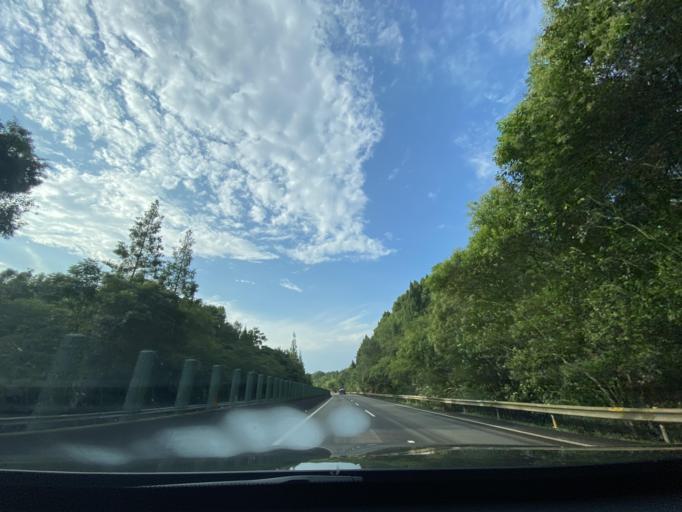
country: CN
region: Sichuan
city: Jiancheng
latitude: 30.3099
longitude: 104.5778
